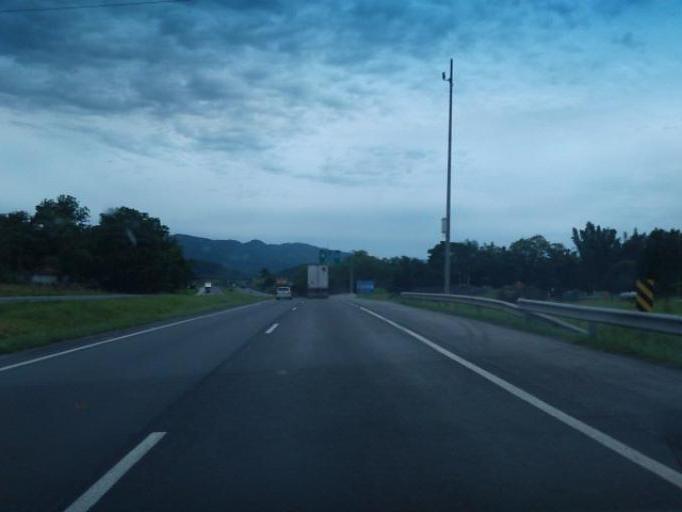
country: BR
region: Sao Paulo
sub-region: Miracatu
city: Miracatu
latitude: -24.2469
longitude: -47.3694
